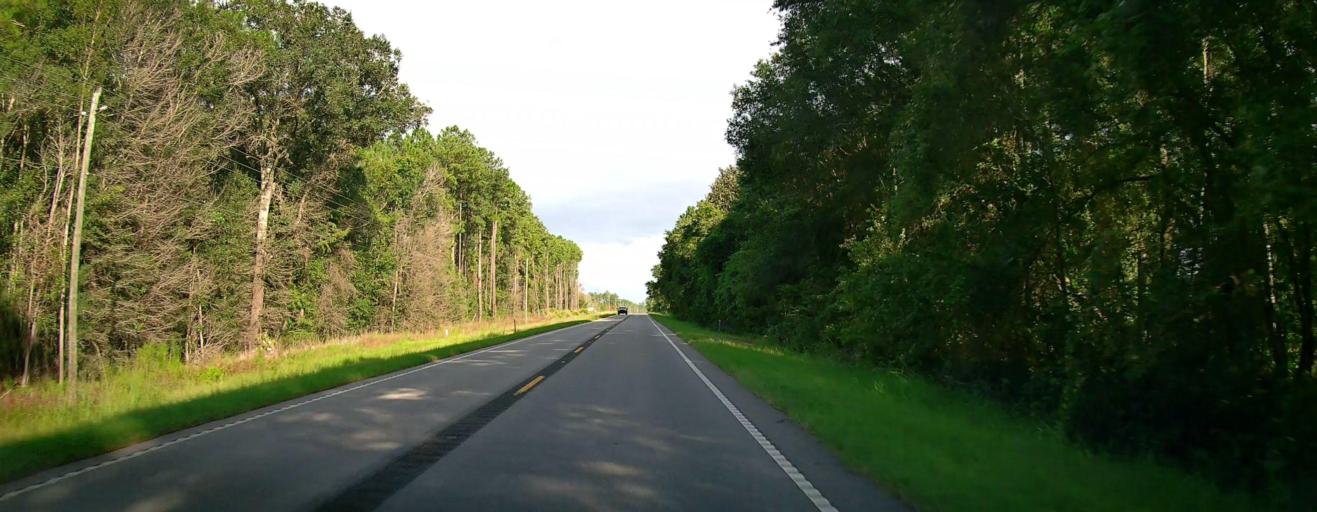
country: US
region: Georgia
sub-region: Coffee County
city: Nicholls
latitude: 31.3902
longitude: -82.6583
